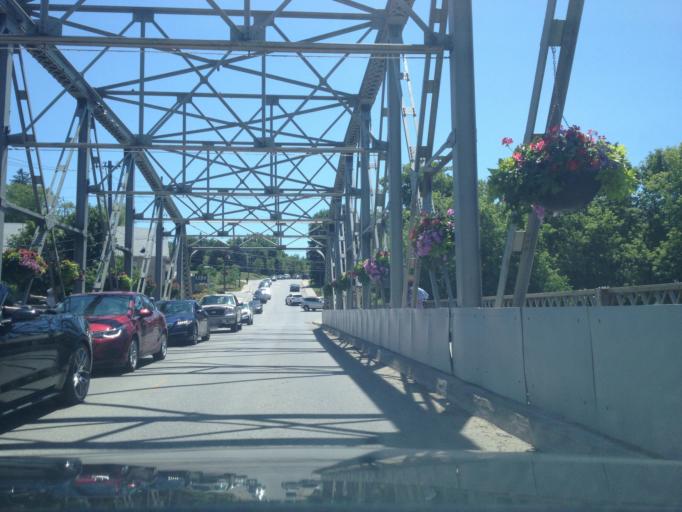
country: CA
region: Ontario
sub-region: Wellington County
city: Guelph
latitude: 43.6807
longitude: -80.4294
